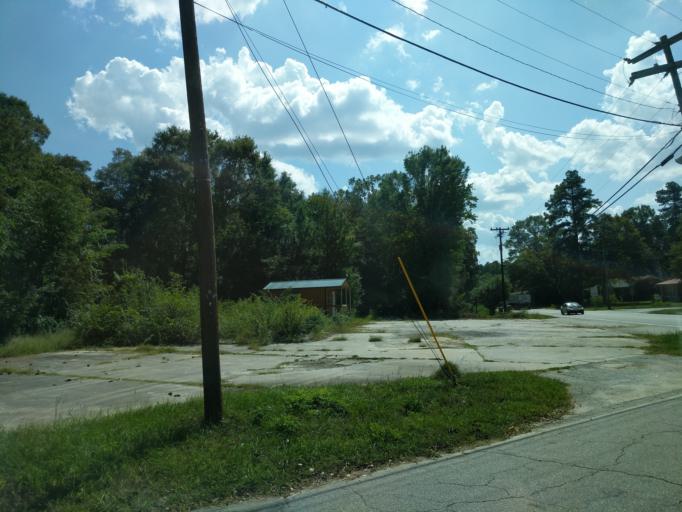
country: US
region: South Carolina
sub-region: Spartanburg County
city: Woodruff
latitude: 34.7357
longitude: -82.0440
